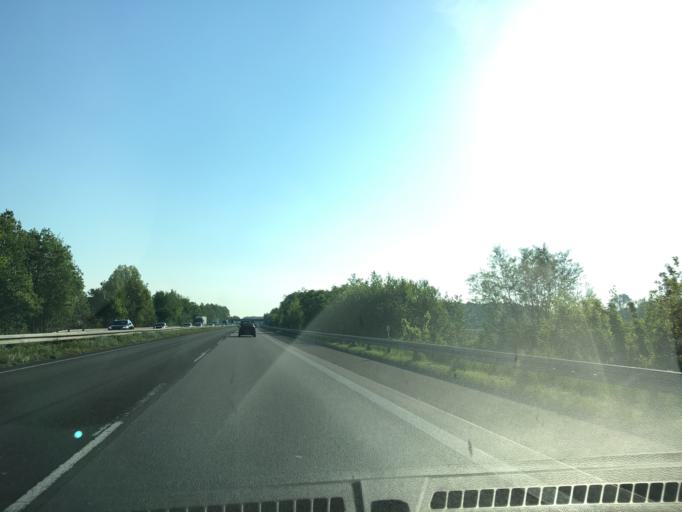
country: DE
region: North Rhine-Westphalia
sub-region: Regierungsbezirk Munster
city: Greven
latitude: 52.0944
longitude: 7.6624
